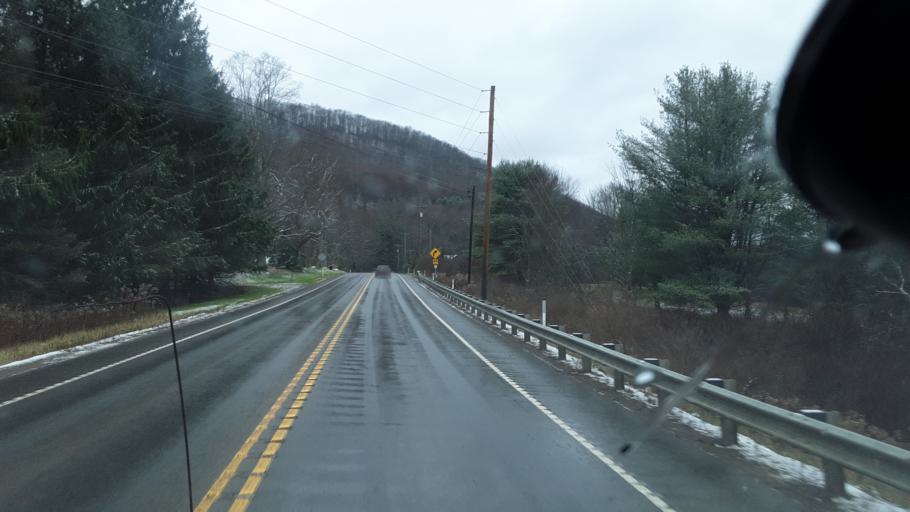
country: US
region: Pennsylvania
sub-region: Potter County
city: Shinglehouse
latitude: 41.9020
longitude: -78.0807
